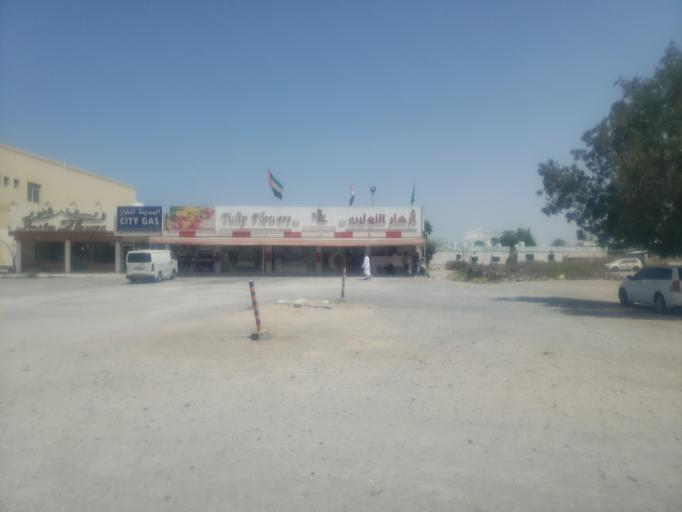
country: AE
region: Ra's al Khaymah
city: Ras al-Khaimah
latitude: 25.8040
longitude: 55.9663
